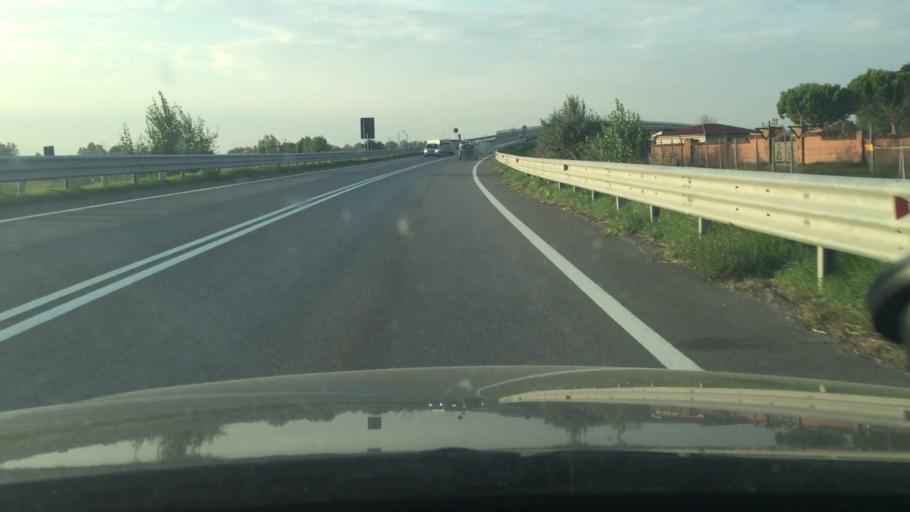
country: IT
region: Emilia-Romagna
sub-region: Provincia di Ferrara
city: Porotto-Cassama
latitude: 44.8367
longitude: 11.5744
